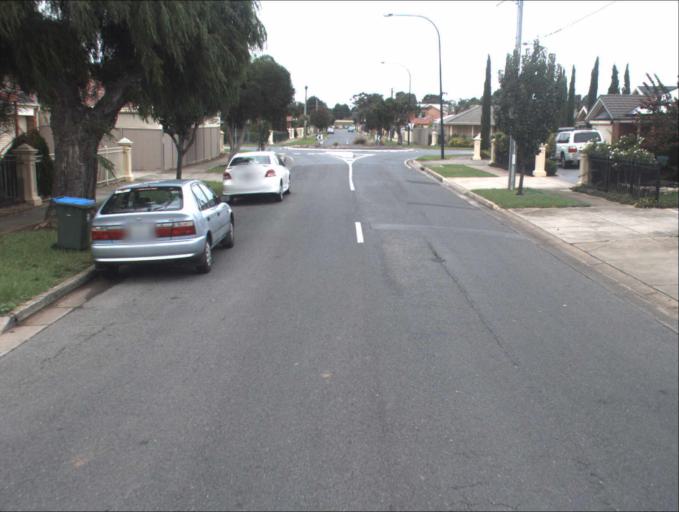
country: AU
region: South Australia
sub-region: Charles Sturt
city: Woodville
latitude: -34.8718
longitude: 138.5614
